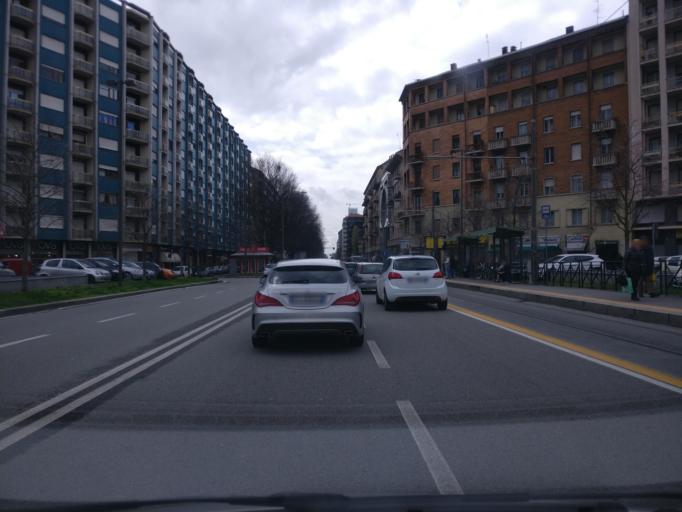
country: IT
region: Piedmont
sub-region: Provincia di Torino
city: Turin
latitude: 45.0421
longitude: 7.6710
